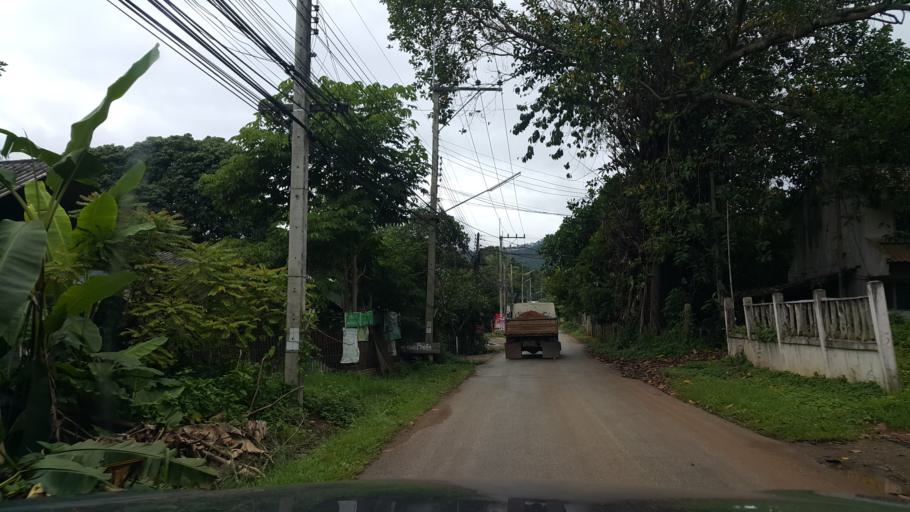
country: TH
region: Chiang Mai
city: Samoeng
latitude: 18.8503
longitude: 98.7320
